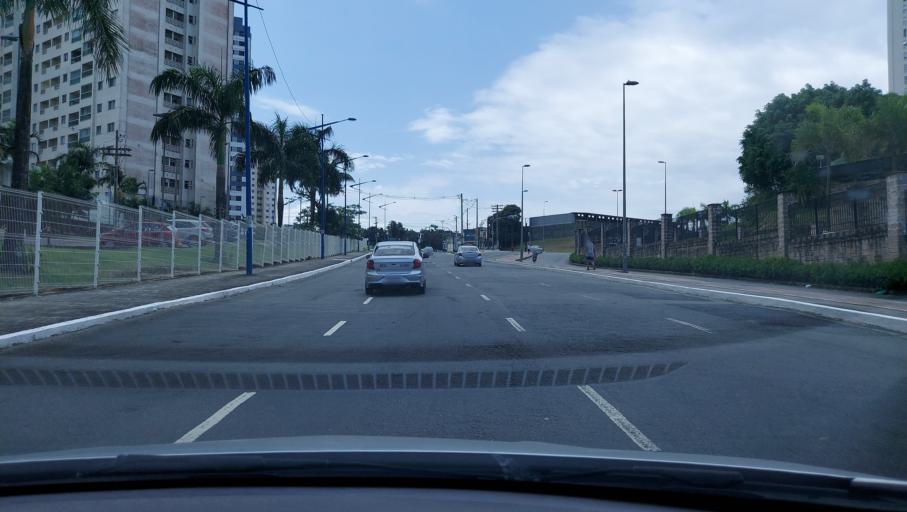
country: BR
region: Bahia
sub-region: Salvador
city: Salvador
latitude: -12.9668
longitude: -38.4747
